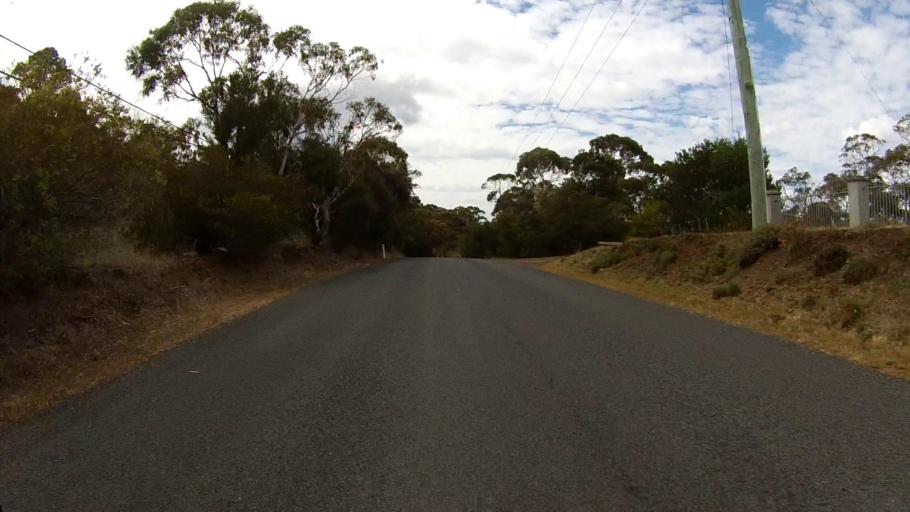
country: AU
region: Tasmania
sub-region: Glenorchy
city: Goodwood
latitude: -42.8001
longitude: 147.2904
